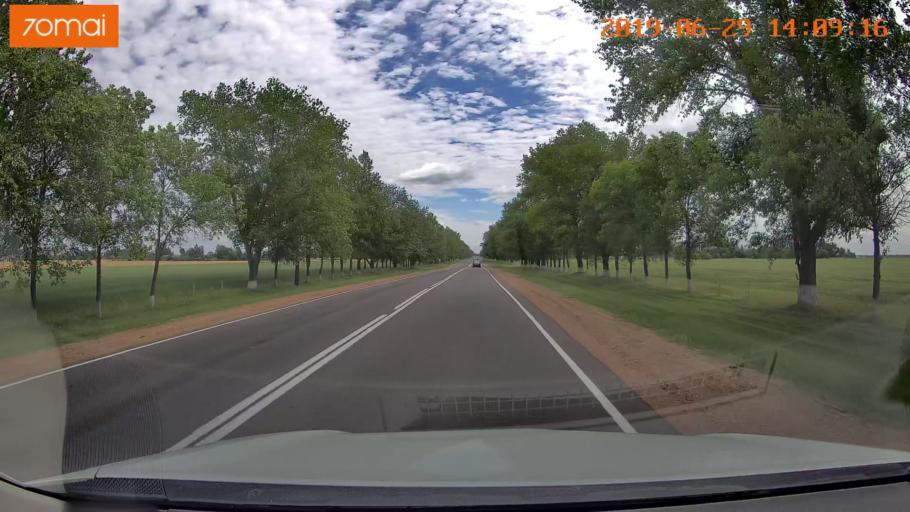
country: BY
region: Minsk
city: Salihorsk
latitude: 52.8419
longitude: 27.4835
